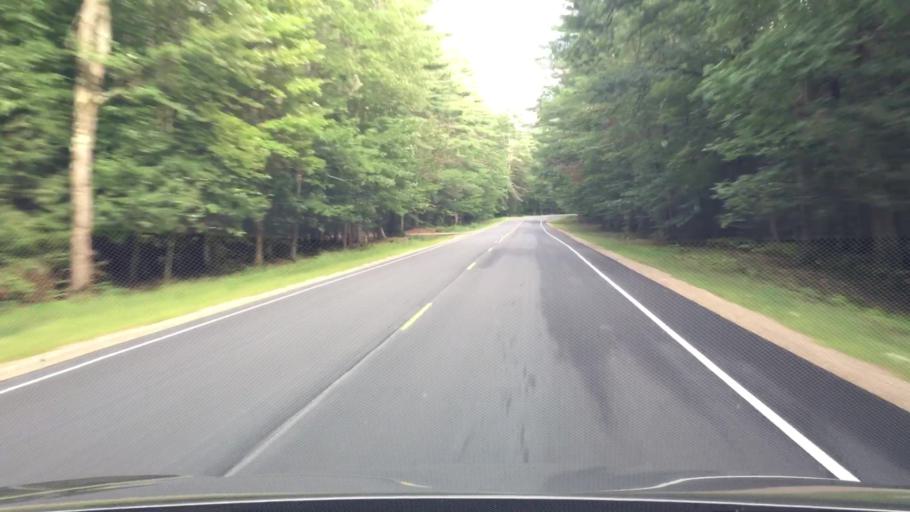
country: US
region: New Hampshire
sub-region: Carroll County
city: Conway
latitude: 43.9857
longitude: -71.1448
